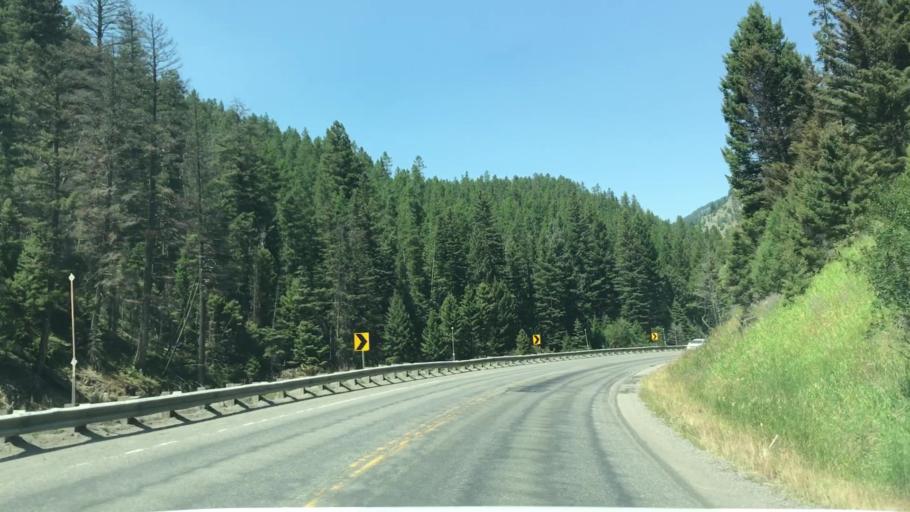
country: US
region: Montana
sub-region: Gallatin County
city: Big Sky
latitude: 45.3825
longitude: -111.1931
